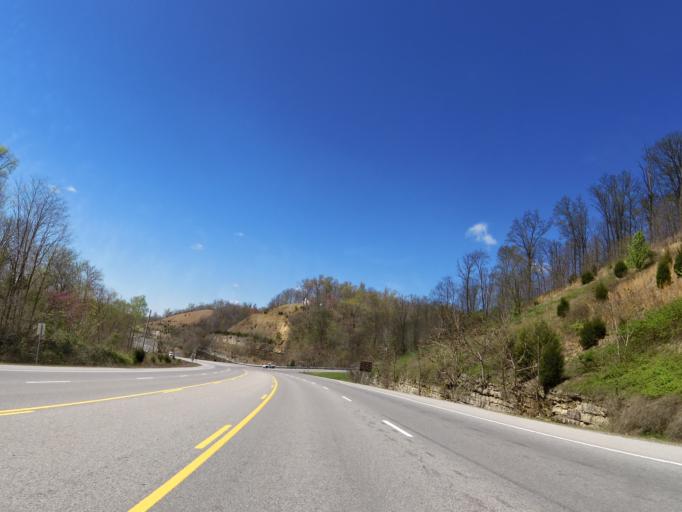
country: US
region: Tennessee
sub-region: DeKalb County
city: Smithville
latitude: 35.9976
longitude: -85.8915
